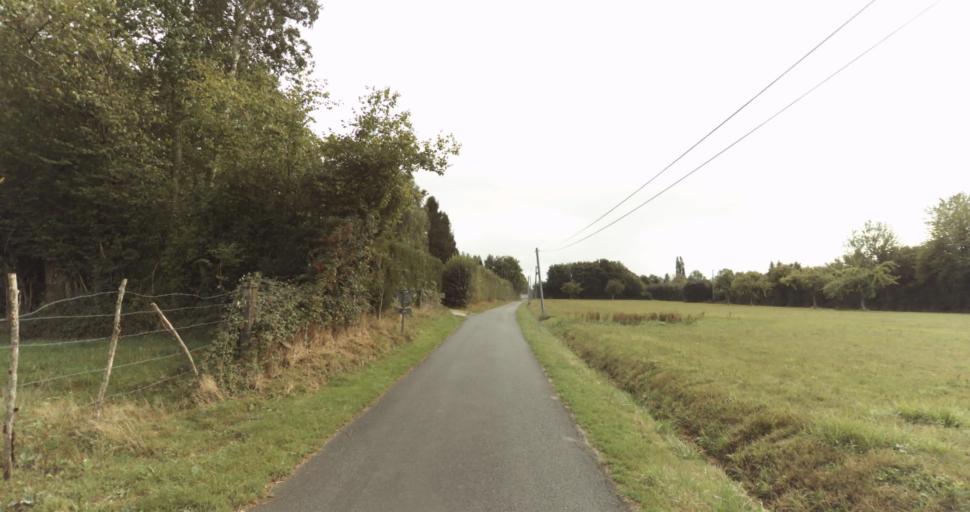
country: FR
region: Lower Normandy
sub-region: Departement de l'Orne
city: Sainte-Gauburge-Sainte-Colombe
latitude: 48.7069
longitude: 0.3870
